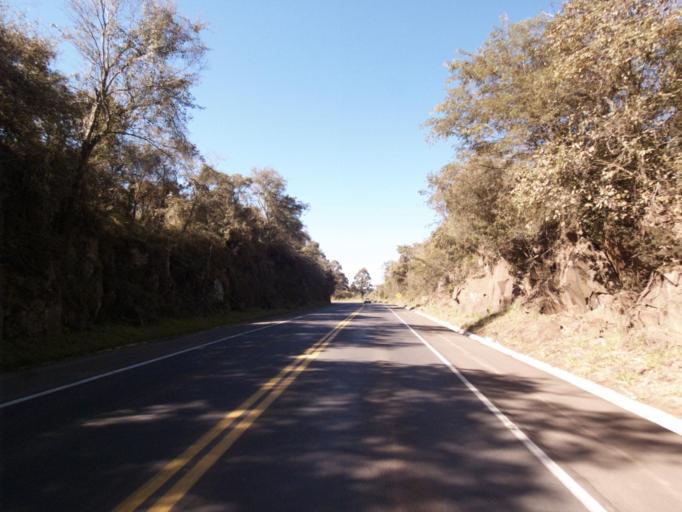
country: BR
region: Santa Catarina
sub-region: Chapeco
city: Chapeco
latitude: -26.9813
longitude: -52.5934
